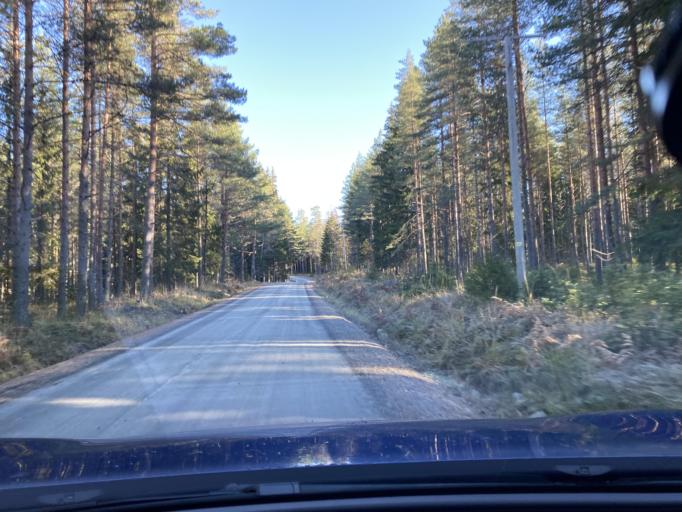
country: FI
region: Haeme
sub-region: Haemeenlinna
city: Kalvola
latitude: 60.9950
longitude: 24.0988
